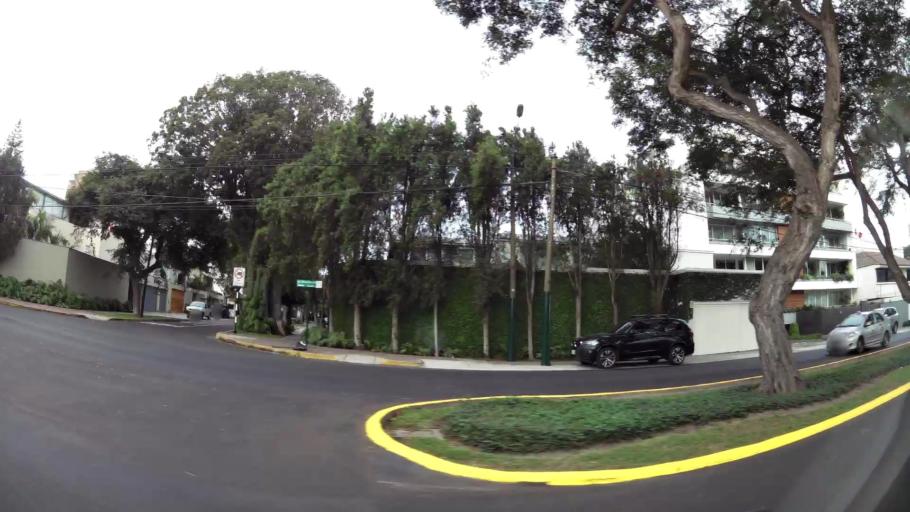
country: PE
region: Lima
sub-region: Lima
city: San Isidro
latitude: -12.1041
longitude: -77.0517
